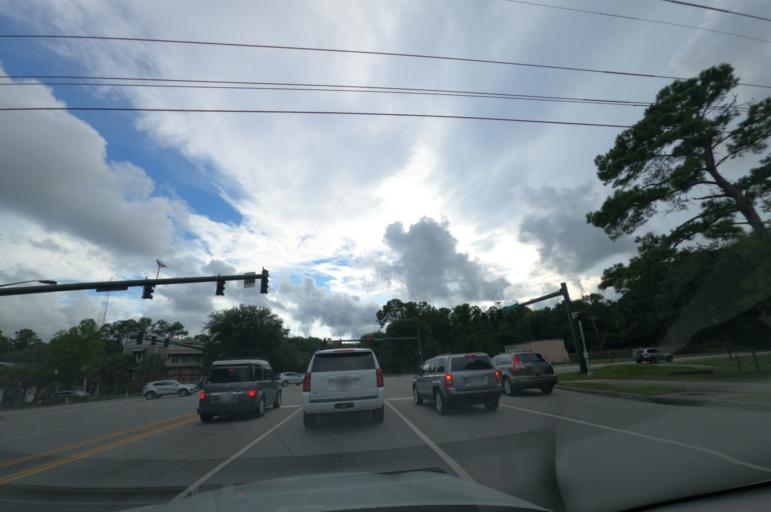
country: US
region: South Carolina
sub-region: Charleston County
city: Mount Pleasant
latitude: 32.8207
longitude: -79.8370
